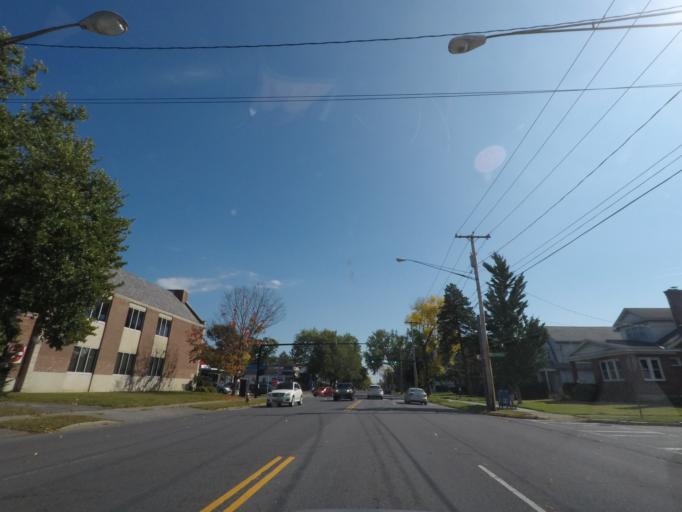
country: US
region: New York
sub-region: Albany County
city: Roessleville
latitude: 42.6769
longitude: -73.7982
